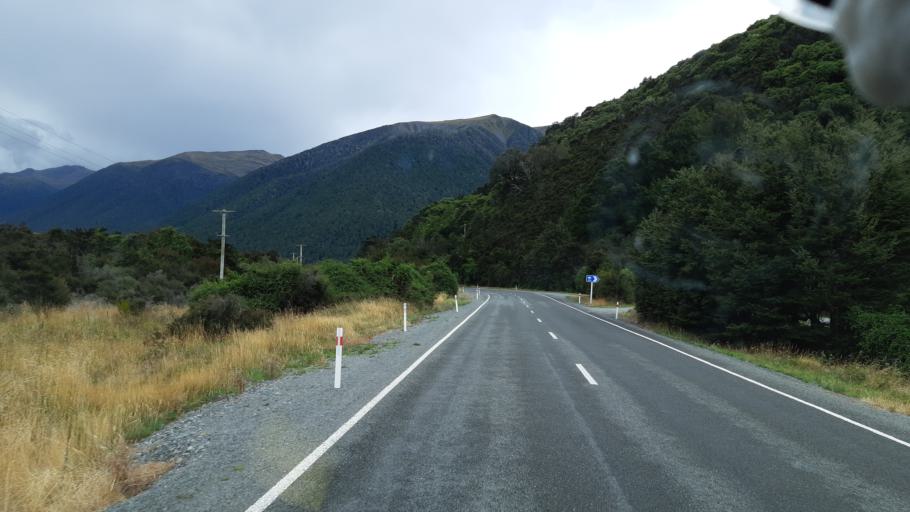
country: NZ
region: Canterbury
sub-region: Hurunui District
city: Amberley
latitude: -42.5587
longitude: 172.3510
